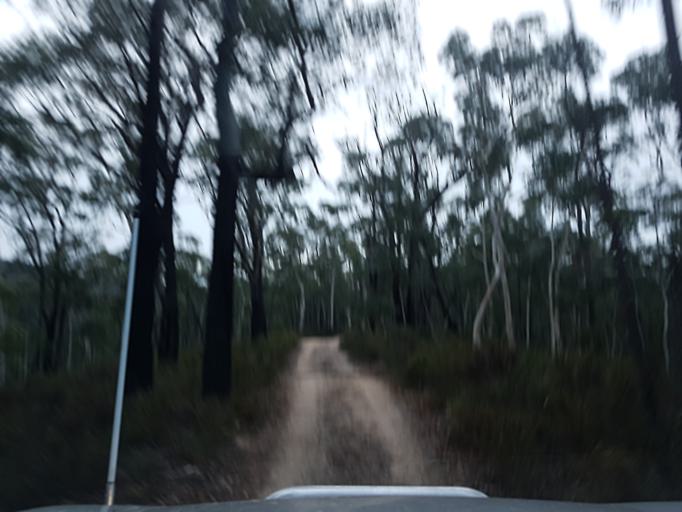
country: AU
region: New South Wales
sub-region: Snowy River
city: Jindabyne
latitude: -36.8606
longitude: 148.2342
